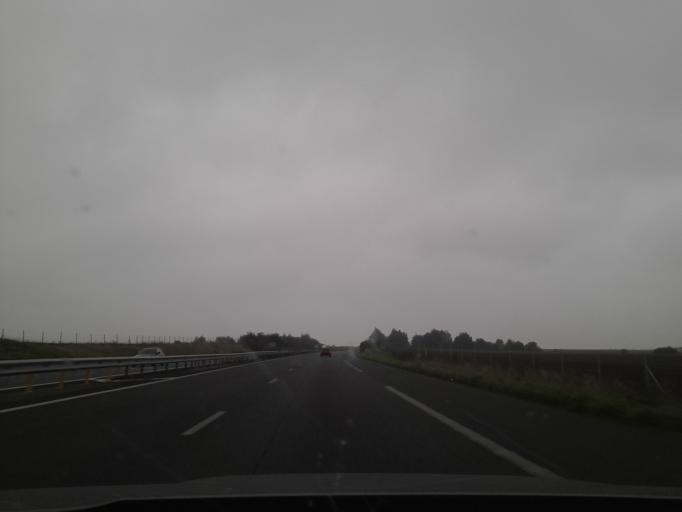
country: FR
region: Nord-Pas-de-Calais
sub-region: Departement du Nord
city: Fontaine-Notre-Dame
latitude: 50.1605
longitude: 3.1664
